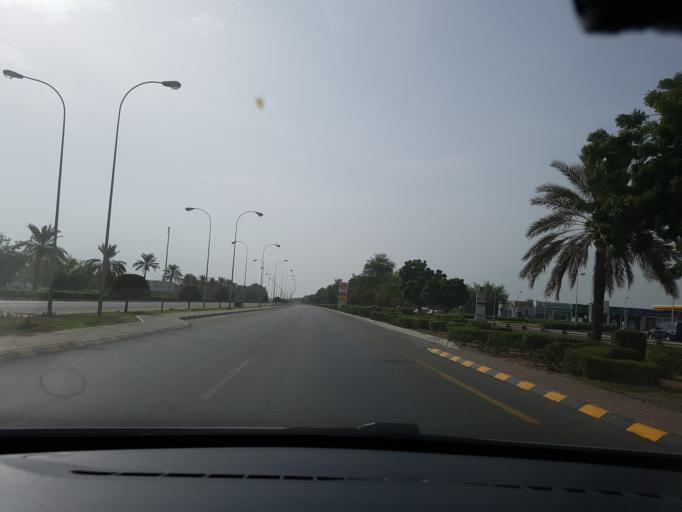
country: OM
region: Al Batinah
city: Al Sohar
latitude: 24.3220
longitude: 56.7491
